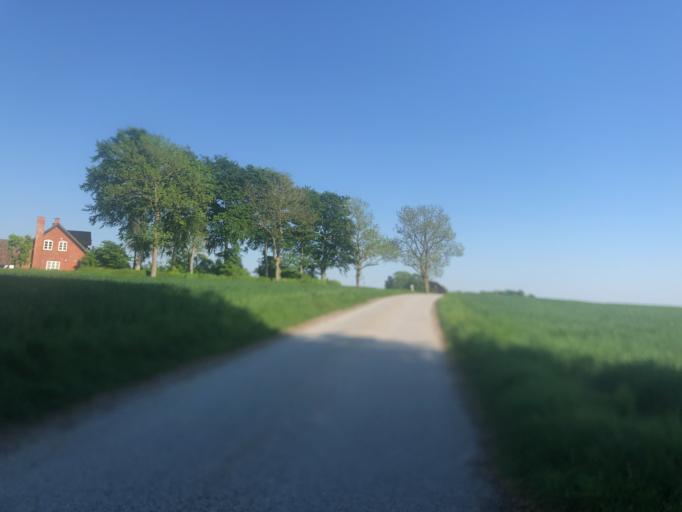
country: DK
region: Zealand
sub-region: Ringsted Kommune
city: Ringsted
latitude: 55.4803
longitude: 11.7938
